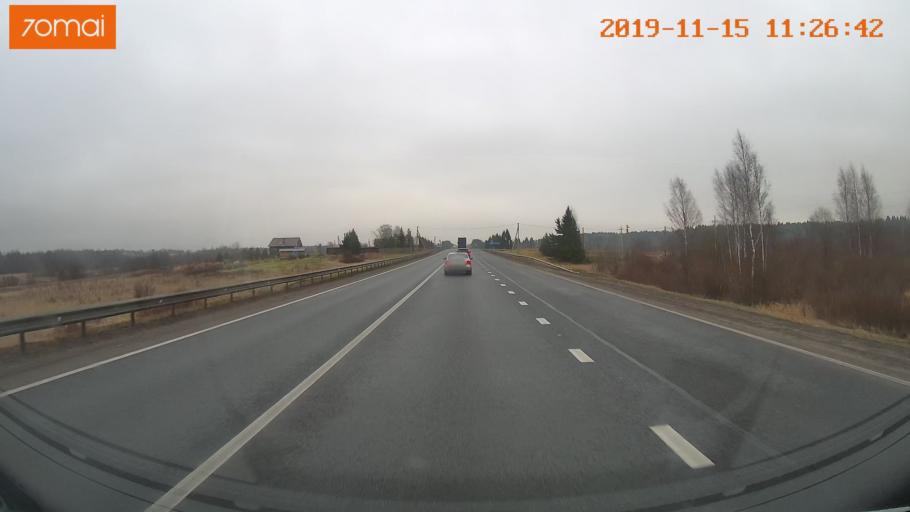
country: RU
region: Vologda
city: Molochnoye
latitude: 59.1676
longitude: 39.4515
